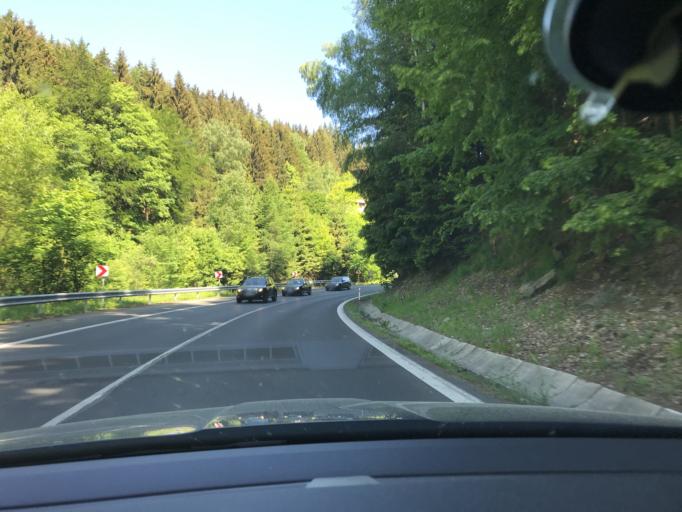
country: CZ
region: Karlovarsky
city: Jachymov
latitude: 50.3502
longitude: 12.9323
